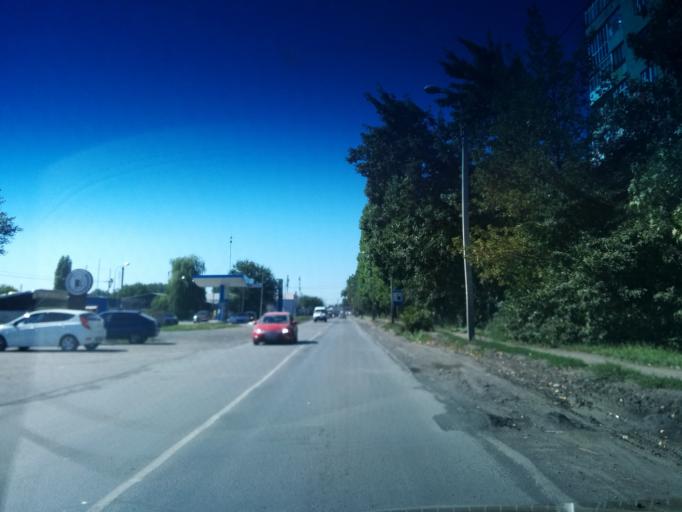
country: RU
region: Rostov
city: Shakhty
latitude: 47.6855
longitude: 40.2705
